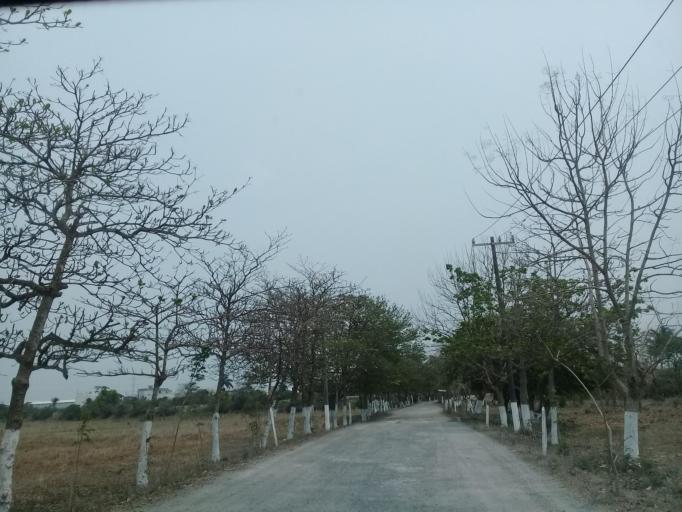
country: MX
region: Veracruz
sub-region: Veracruz
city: Las Amapolas
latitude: 19.1653
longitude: -96.2086
